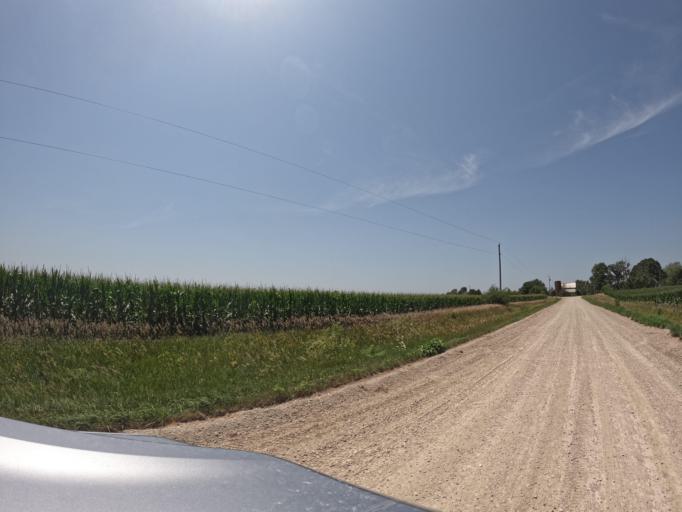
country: US
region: Iowa
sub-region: Henry County
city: Mount Pleasant
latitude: 40.9131
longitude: -91.6441
